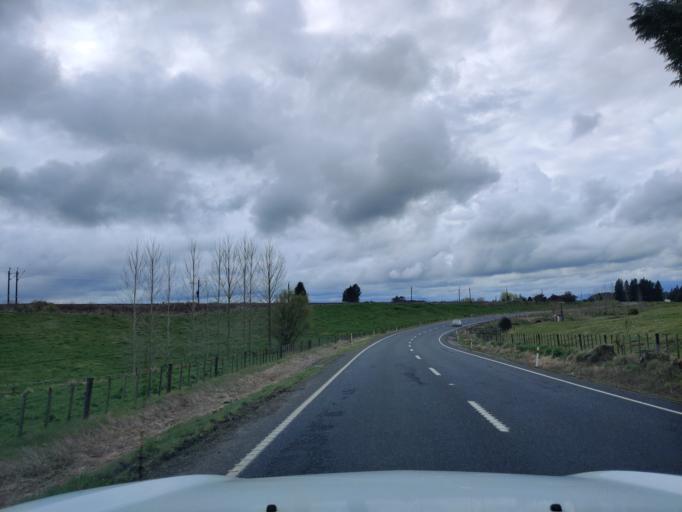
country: NZ
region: Waikato
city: Turangi
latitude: -39.0329
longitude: 175.3820
